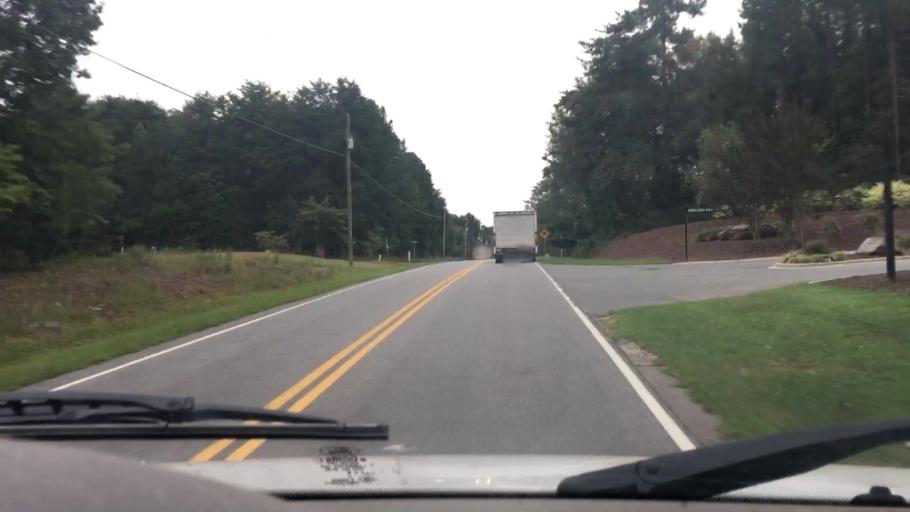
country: US
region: North Carolina
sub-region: Catawba County
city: Lake Norman of Catawba
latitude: 35.5618
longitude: -80.9904
